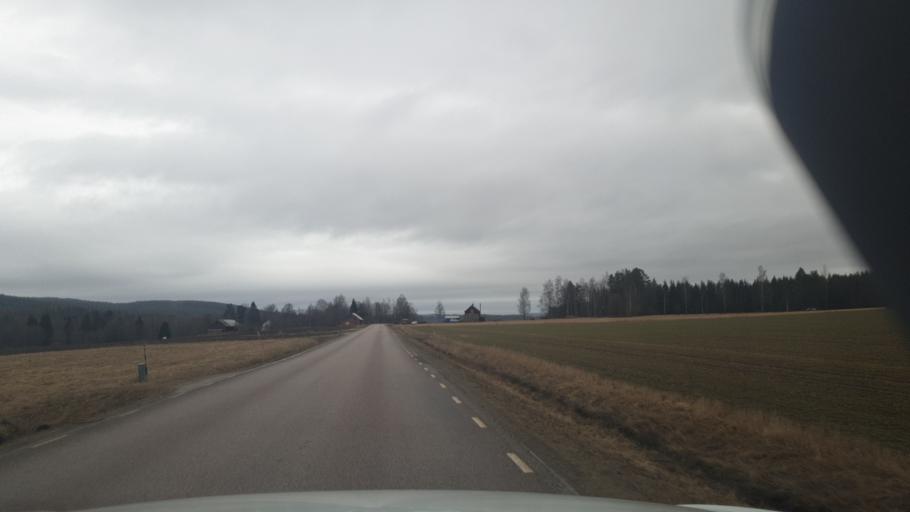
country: SE
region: Vaermland
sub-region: Eda Kommun
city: Charlottenberg
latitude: 59.7555
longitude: 12.1577
